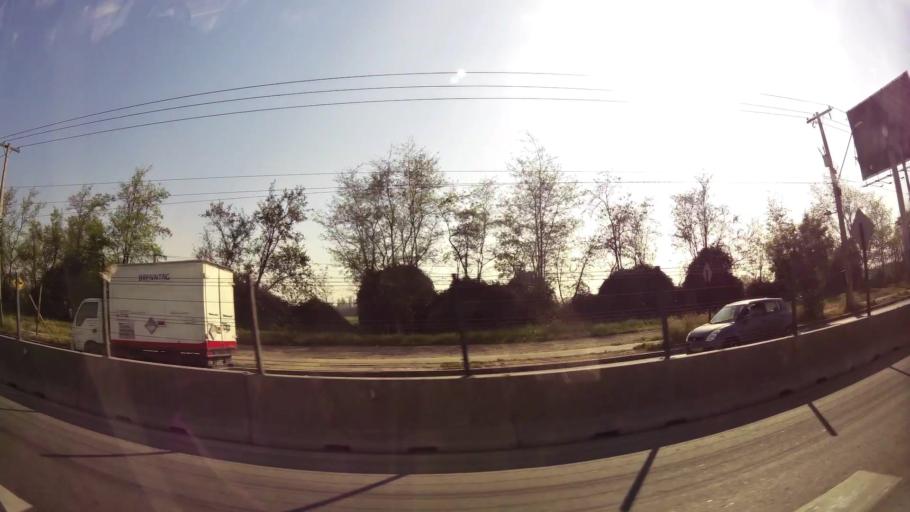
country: CL
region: Santiago Metropolitan
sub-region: Provincia de Santiago
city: Lo Prado
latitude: -33.5158
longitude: -70.7144
